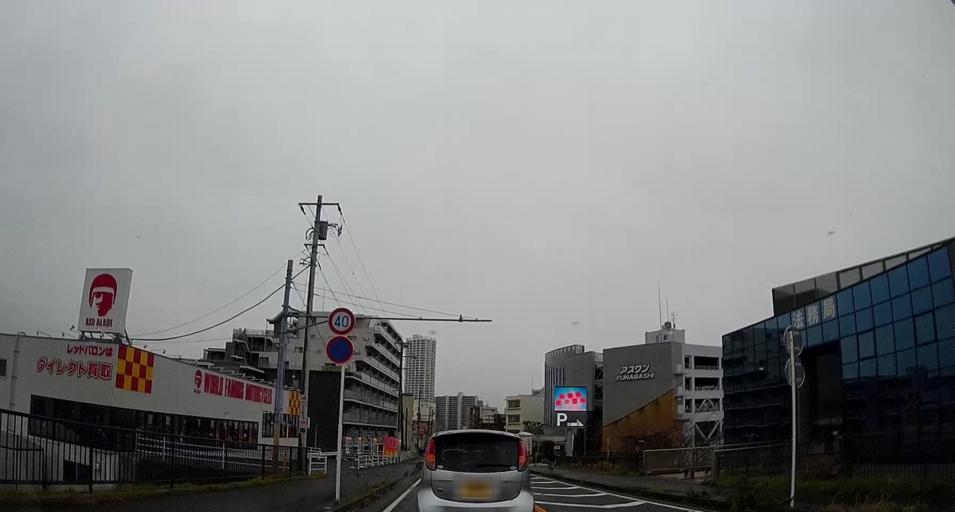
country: JP
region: Chiba
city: Funabashi
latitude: 35.7011
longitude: 139.9754
